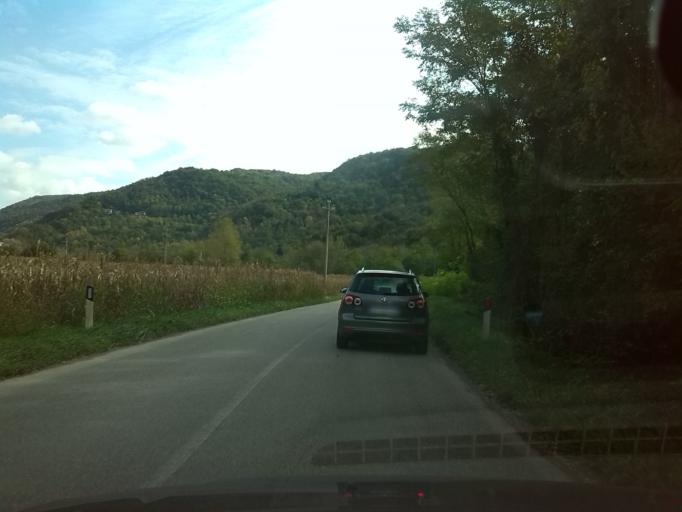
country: IT
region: Friuli Venezia Giulia
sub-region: Provincia di Udine
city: San Leonardo
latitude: 46.1210
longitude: 13.5341
